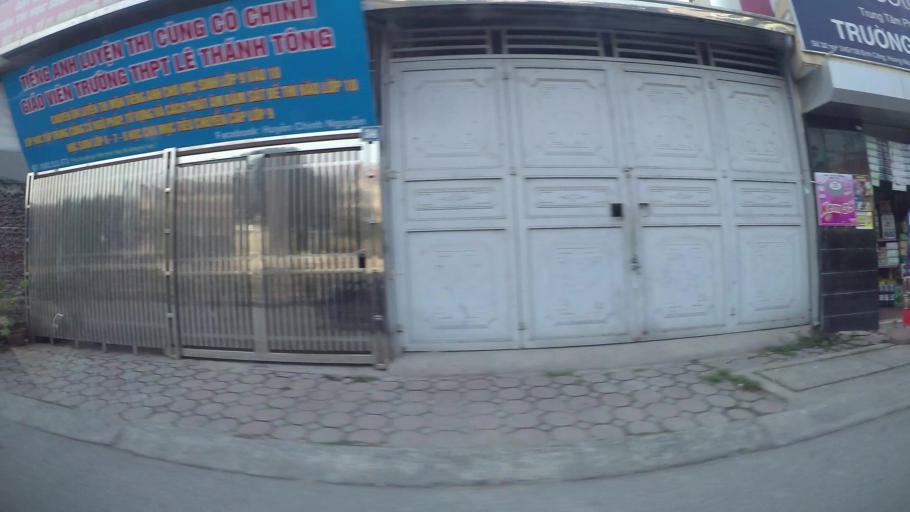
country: VN
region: Ha Noi
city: Van Dien
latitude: 20.9771
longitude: 105.8335
